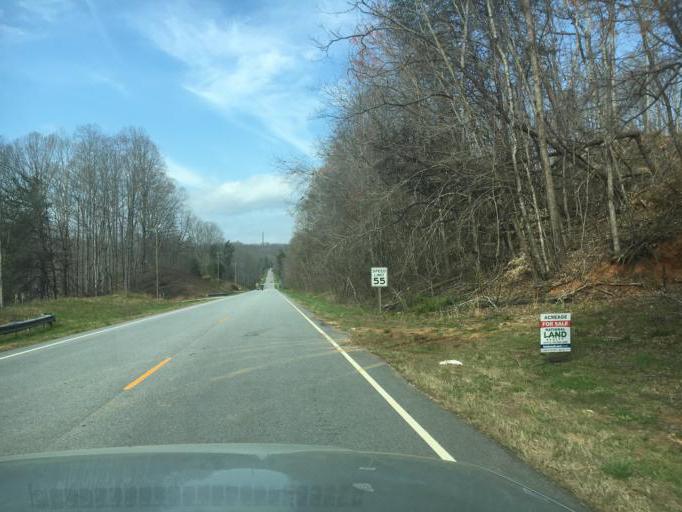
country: US
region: South Carolina
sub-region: Greenville County
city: Tigerville
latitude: 35.1054
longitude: -82.3693
